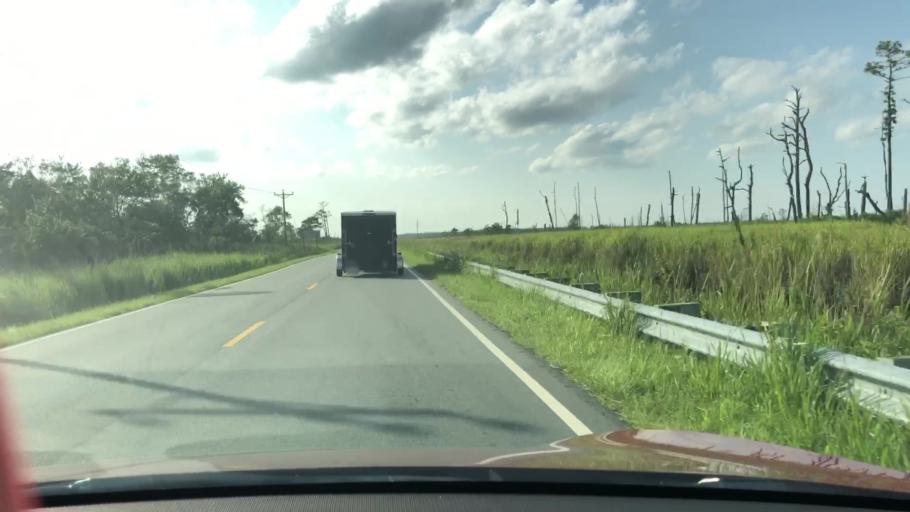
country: US
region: North Carolina
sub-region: Dare County
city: Wanchese
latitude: 35.6217
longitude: -75.8401
